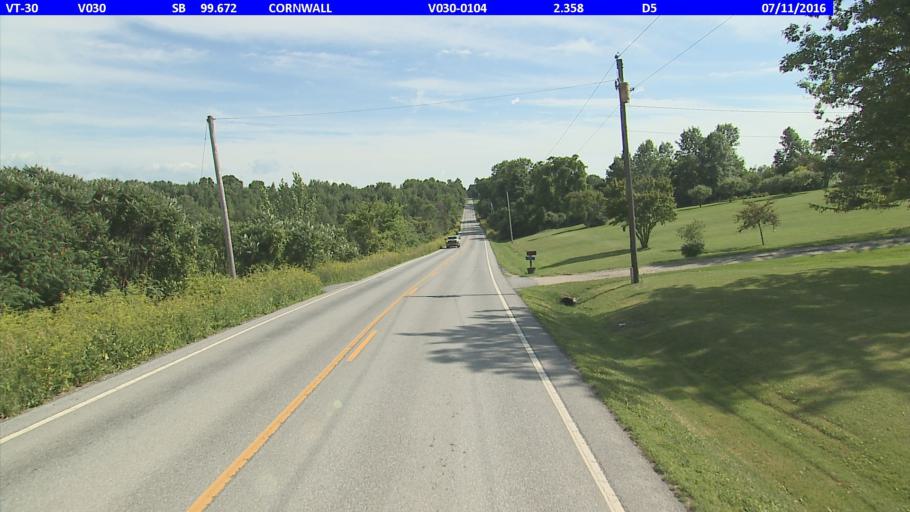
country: US
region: Vermont
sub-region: Addison County
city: Middlebury (village)
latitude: 43.9417
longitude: -73.2118
